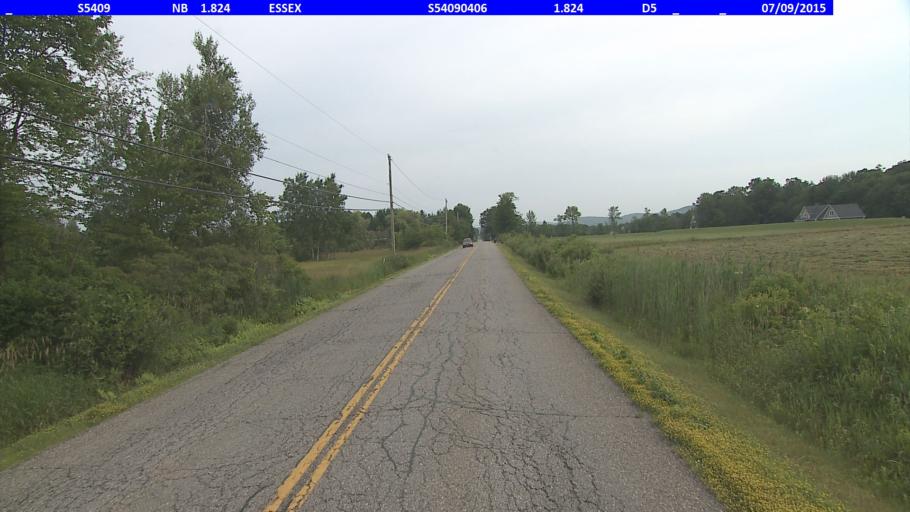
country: US
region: Vermont
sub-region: Chittenden County
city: Essex Junction
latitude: 44.5353
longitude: -73.0750
